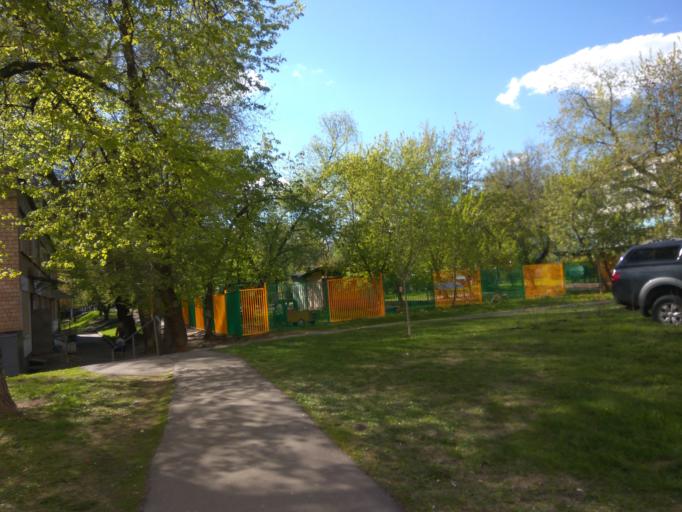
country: RU
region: Moscow
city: Kolomenskoye
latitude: 55.6773
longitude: 37.6751
